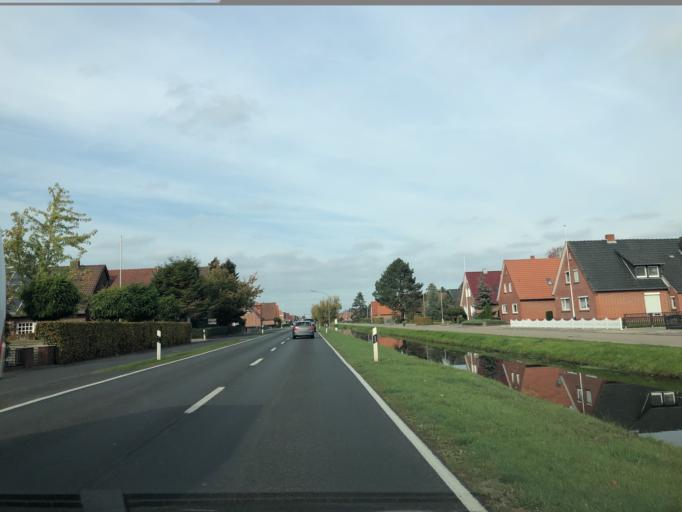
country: DE
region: Lower Saxony
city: Papenburg
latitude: 53.0556
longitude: 7.4559
